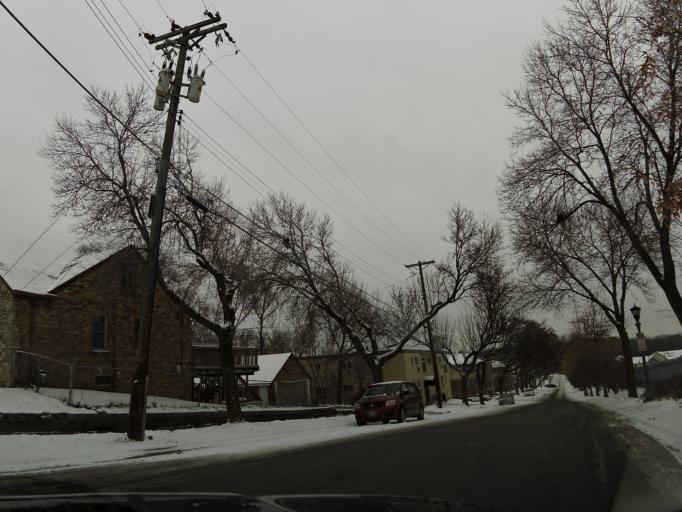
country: US
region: Minnesota
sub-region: Ramsey County
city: Maplewood
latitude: 44.9775
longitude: -93.0384
